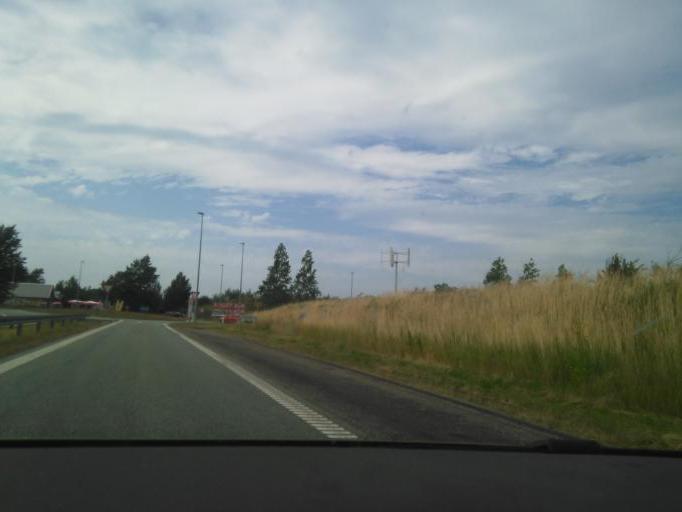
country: DK
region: Zealand
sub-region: Slagelse Kommune
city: Korsor
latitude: 55.3492
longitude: 11.1243
